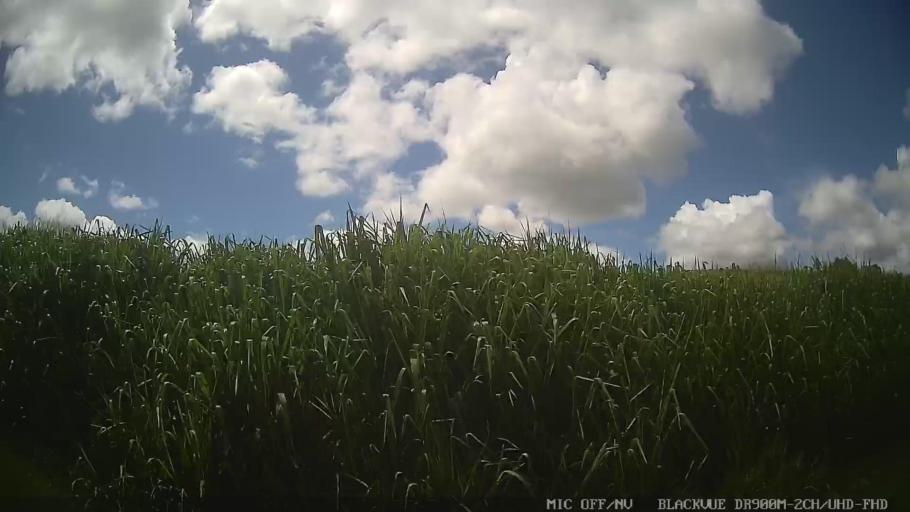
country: BR
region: Sao Paulo
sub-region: Amparo
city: Amparo
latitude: -22.8452
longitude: -46.7153
